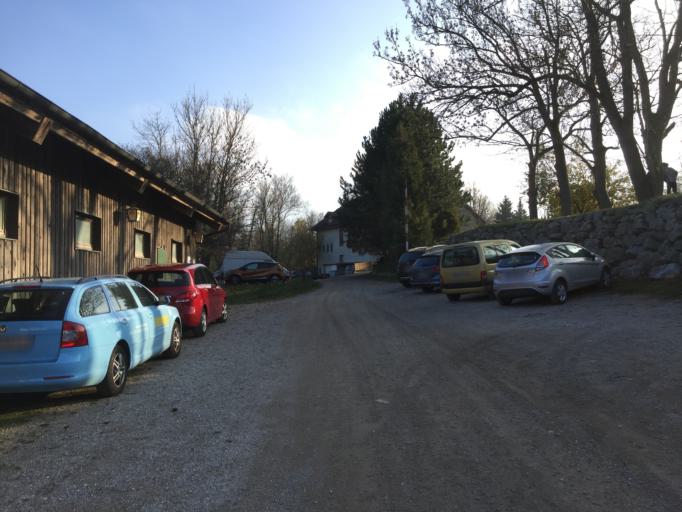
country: AT
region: Lower Austria
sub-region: Politischer Bezirk Wien-Umgebung
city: Gablitz
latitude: 48.2183
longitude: 16.1537
